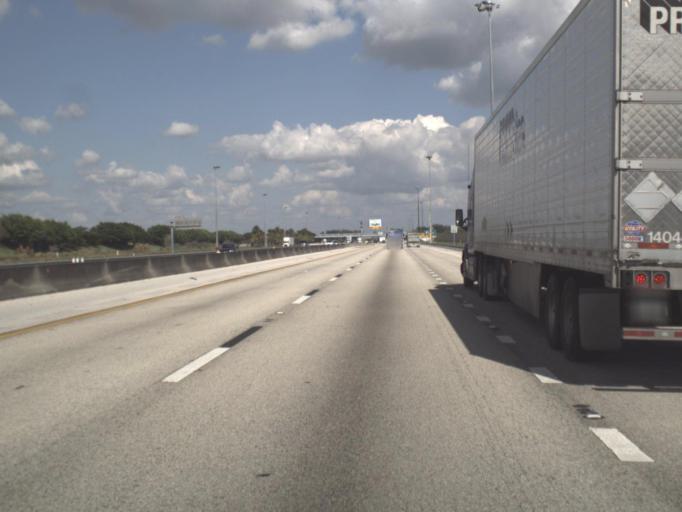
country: US
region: Florida
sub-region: Palm Beach County
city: Seminole Manor
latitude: 26.5555
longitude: -80.1729
